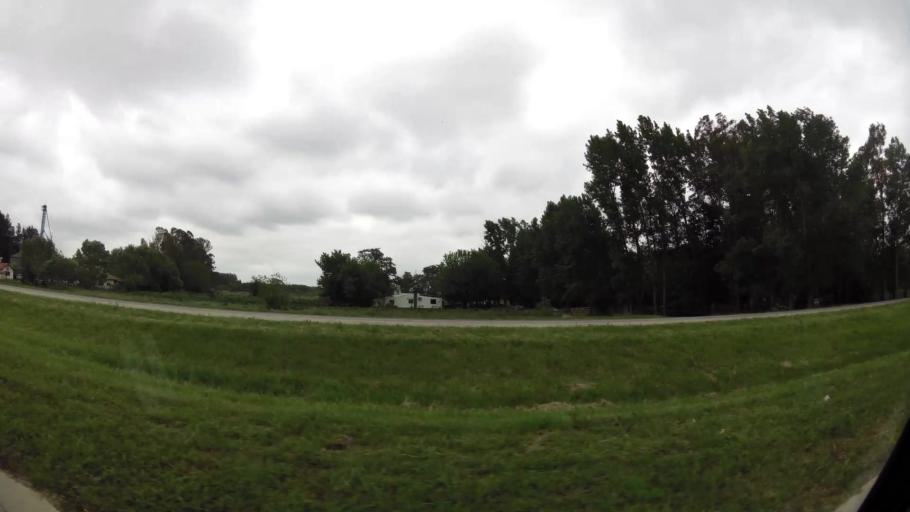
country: AR
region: Buenos Aires
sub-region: Partido de San Vicente
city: San Vicente
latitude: -35.0524
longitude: -58.4354
